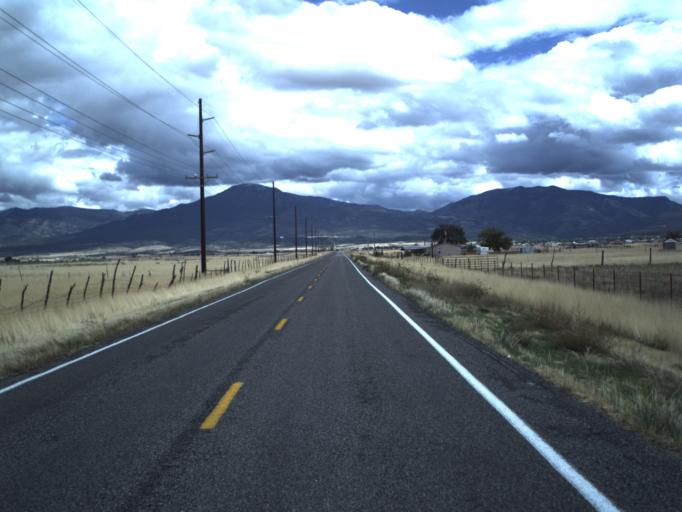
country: US
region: Utah
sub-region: Millard County
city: Fillmore
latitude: 38.9792
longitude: -112.3966
